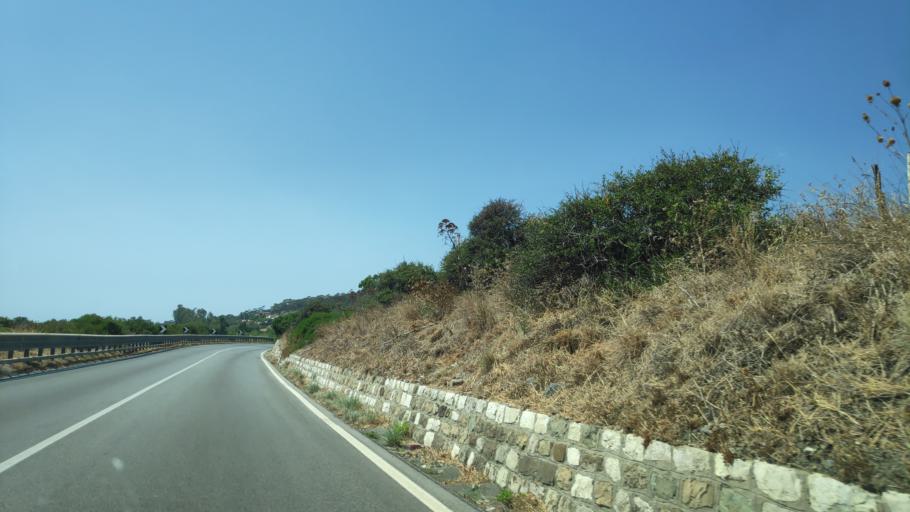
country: IT
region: Calabria
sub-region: Provincia di Reggio Calabria
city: Brancaleone-Marina
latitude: 38.0030
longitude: 16.1263
